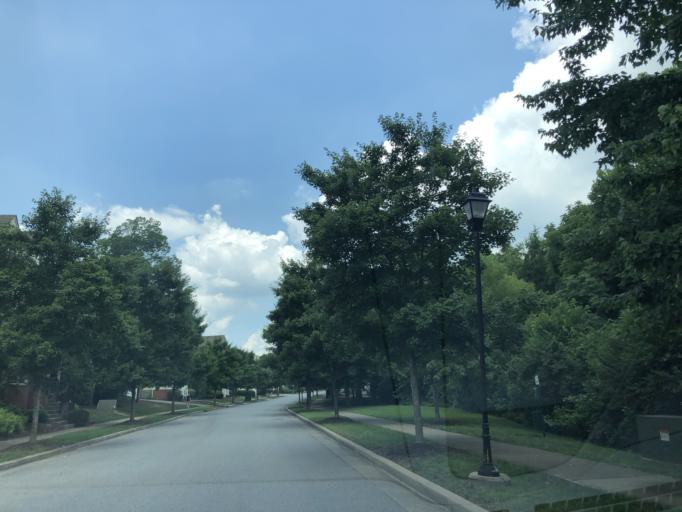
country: US
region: Tennessee
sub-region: Williamson County
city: Brentwood Estates
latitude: 36.0206
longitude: -86.7049
